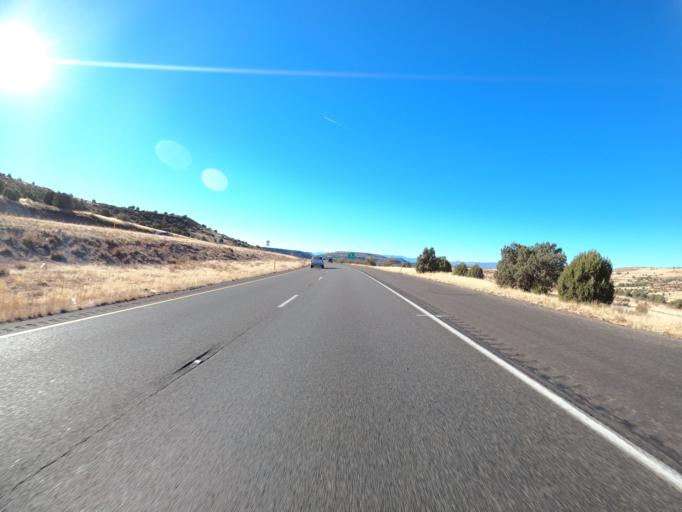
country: US
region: Arizona
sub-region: Yavapai County
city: Camp Verde
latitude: 34.5309
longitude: -111.9806
